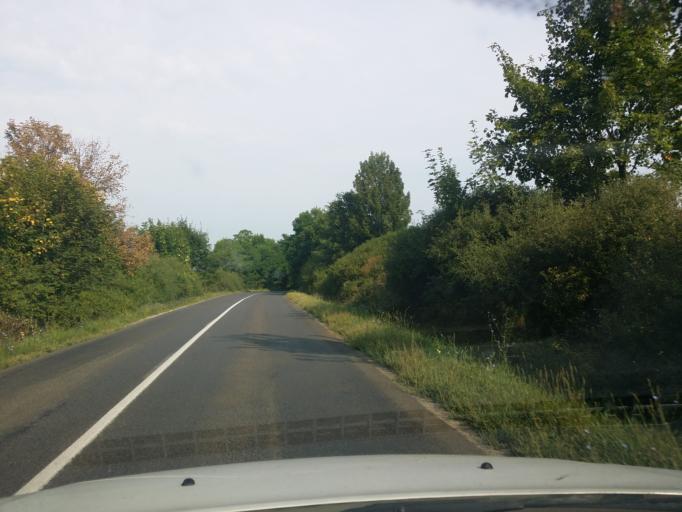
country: HU
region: Pest
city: Galgamacsa
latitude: 47.7144
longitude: 19.3836
